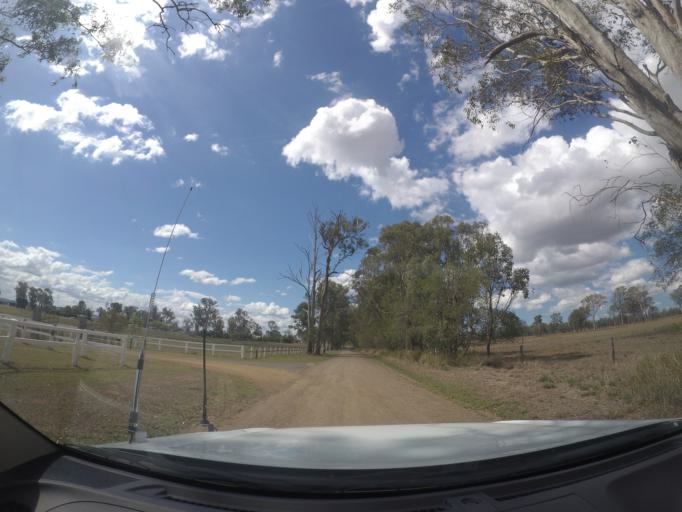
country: AU
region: Queensland
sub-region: Logan
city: Cedar Vale
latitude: -27.8873
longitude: 152.9602
